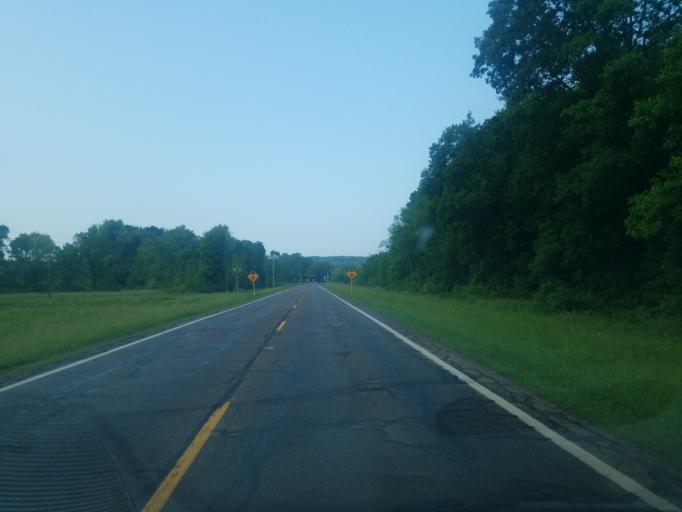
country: US
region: Ohio
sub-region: Tuscarawas County
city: Rockford
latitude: 40.5155
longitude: -81.2618
